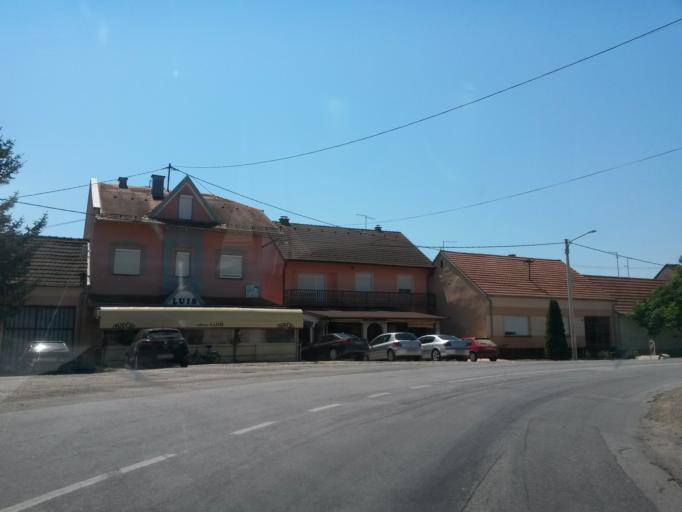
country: HR
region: Brodsko-Posavska
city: Krusevica
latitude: 45.0759
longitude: 18.4848
